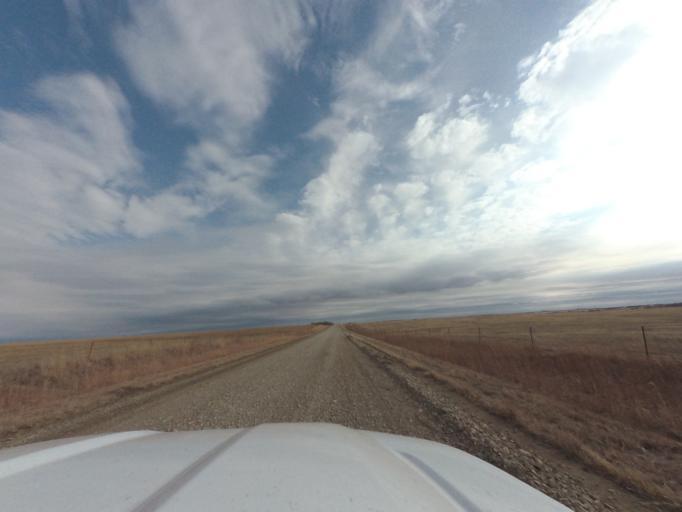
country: US
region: Kansas
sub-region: Chase County
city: Cottonwood Falls
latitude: 38.2171
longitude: -96.7155
